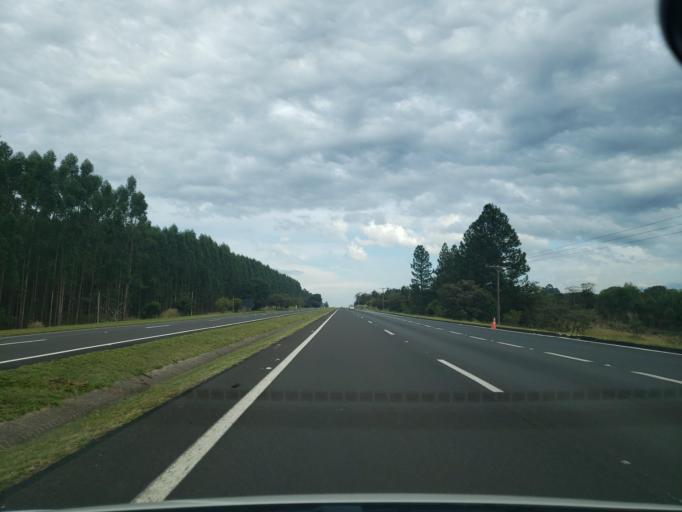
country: BR
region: Sao Paulo
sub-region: Itirapina
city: Itirapina
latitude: -22.2585
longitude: -47.8681
